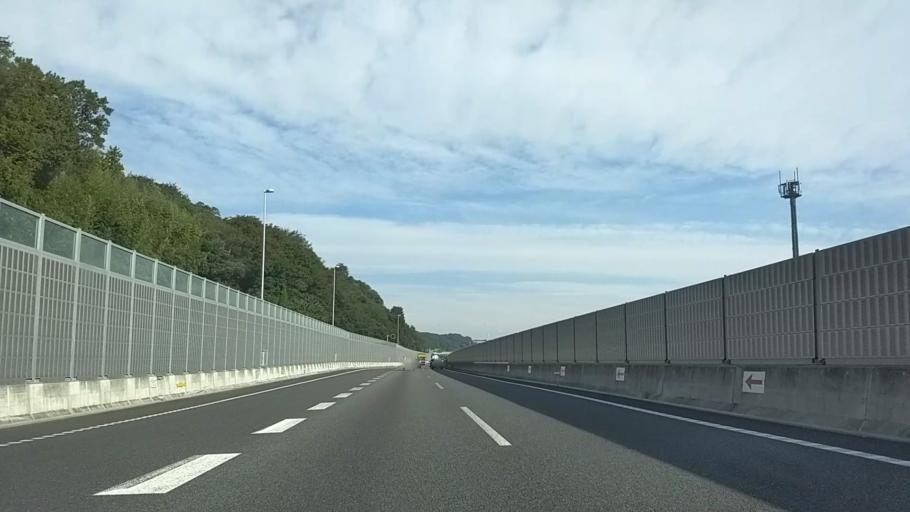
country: JP
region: Kanagawa
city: Zama
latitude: 35.4907
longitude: 139.3689
